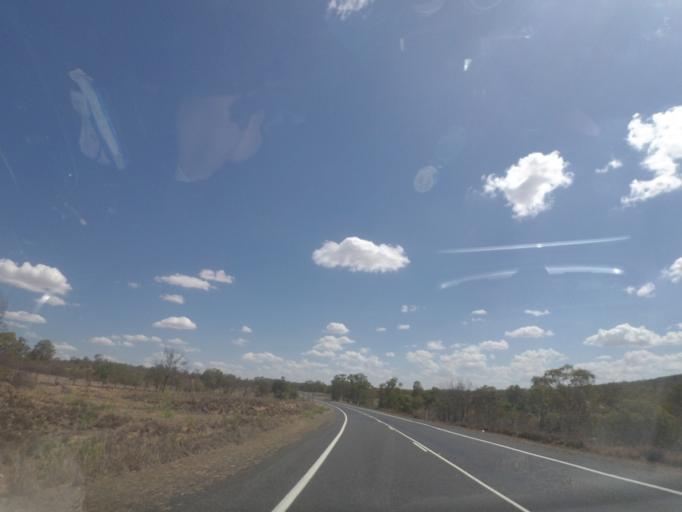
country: AU
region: Queensland
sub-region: Southern Downs
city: Warwick
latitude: -28.2219
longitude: 151.5539
